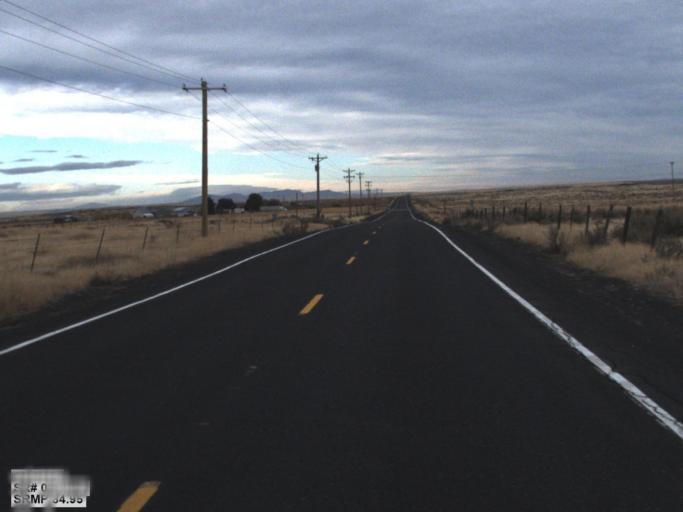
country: US
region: Washington
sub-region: Okanogan County
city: Coulee Dam
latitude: 47.6685
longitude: -118.7216
